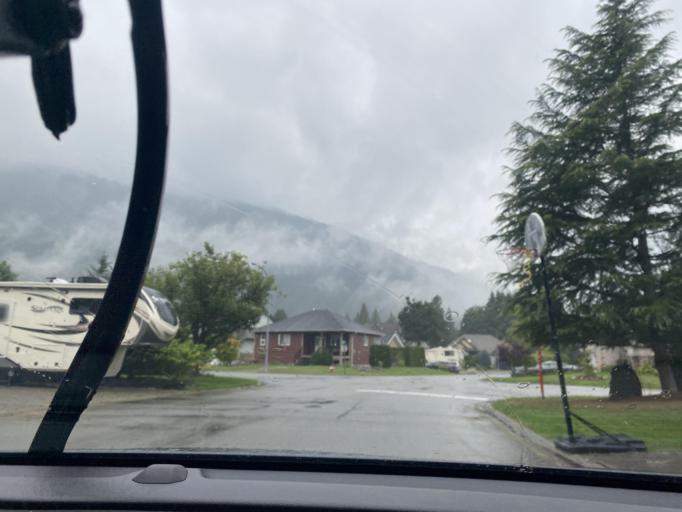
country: CA
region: British Columbia
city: Agassiz
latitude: 49.2984
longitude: -121.7757
